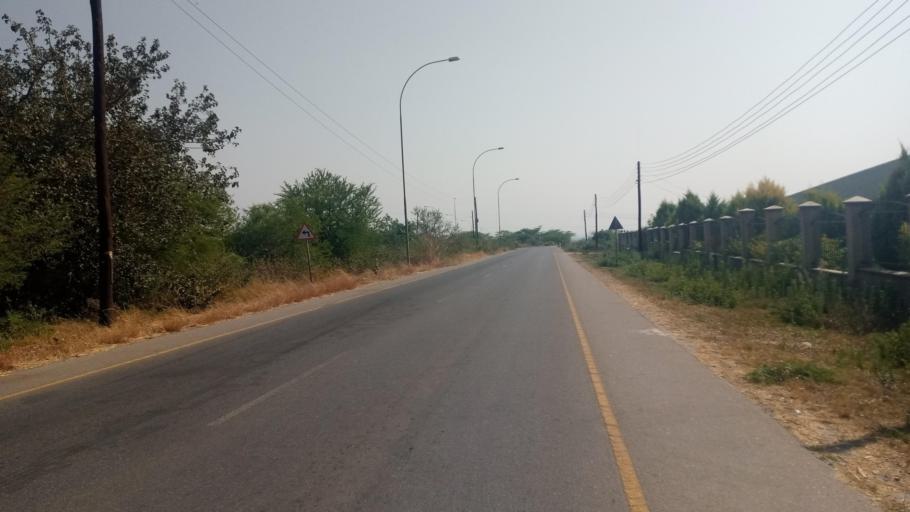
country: ZM
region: Lusaka
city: Lusaka
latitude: -15.4534
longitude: 28.4353
